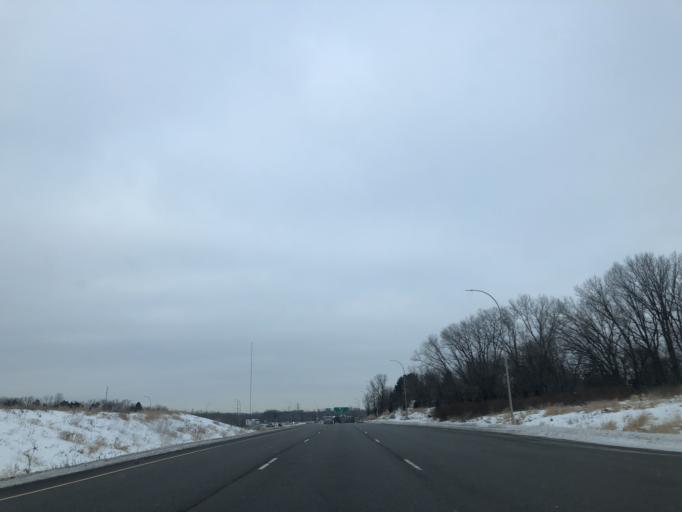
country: US
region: Minnesota
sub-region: Ramsey County
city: Arden Hills
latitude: 45.0636
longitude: -93.1588
